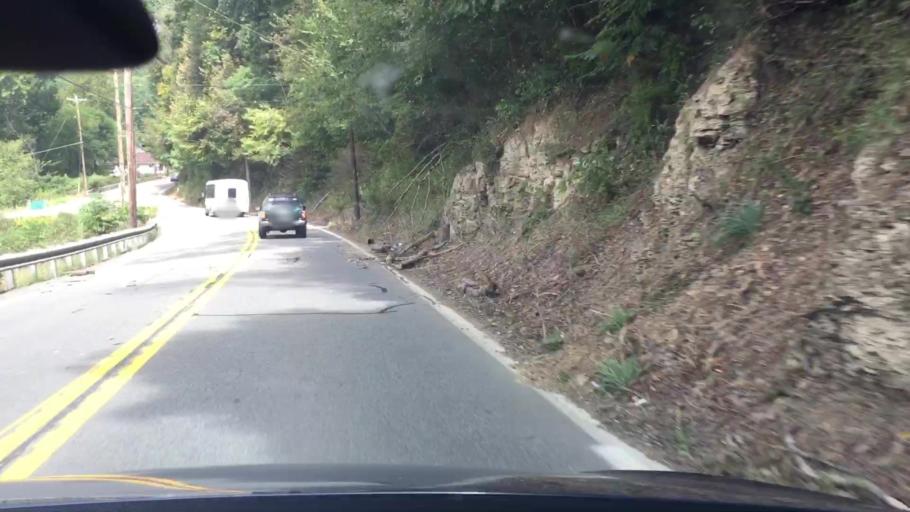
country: US
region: Pennsylvania
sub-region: Allegheny County
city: Cheswick
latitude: 40.5166
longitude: -79.8055
